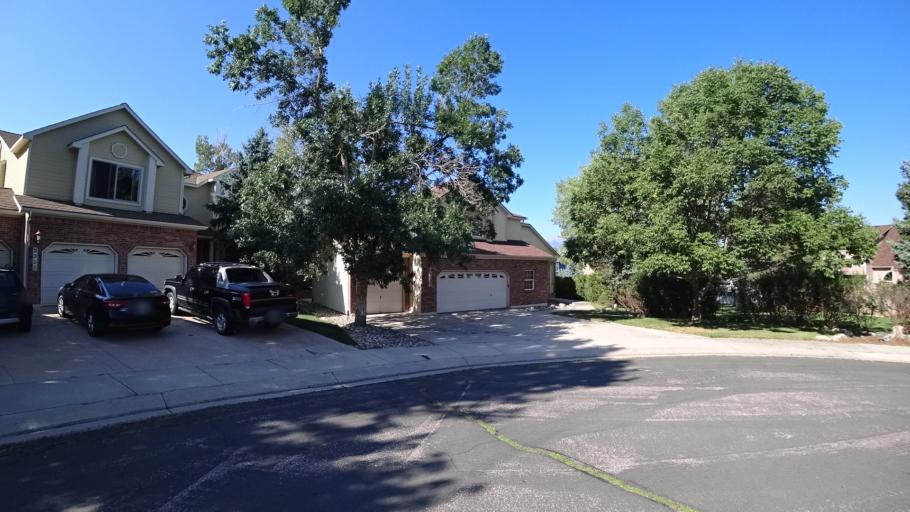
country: US
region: Colorado
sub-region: El Paso County
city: Colorado Springs
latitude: 38.8874
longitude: -104.7823
